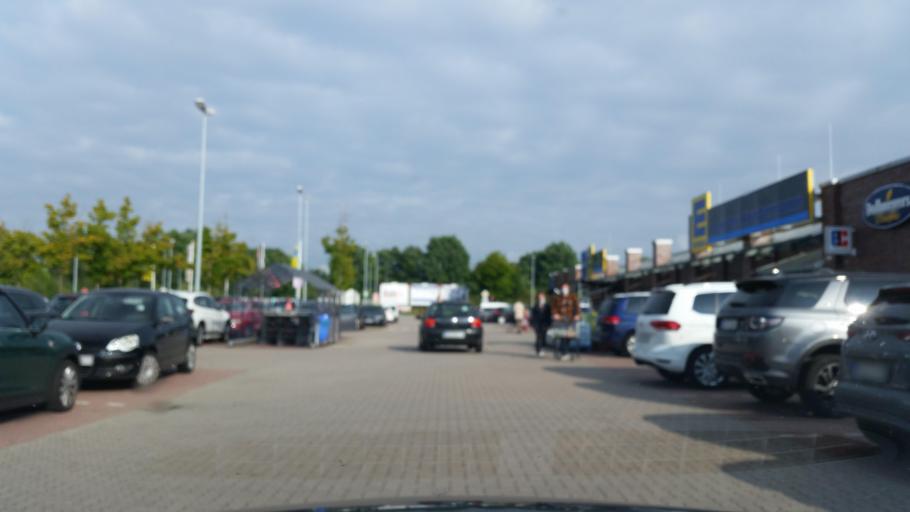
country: DE
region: Schleswig-Holstein
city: Reinbek
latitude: 53.5283
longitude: 10.2507
